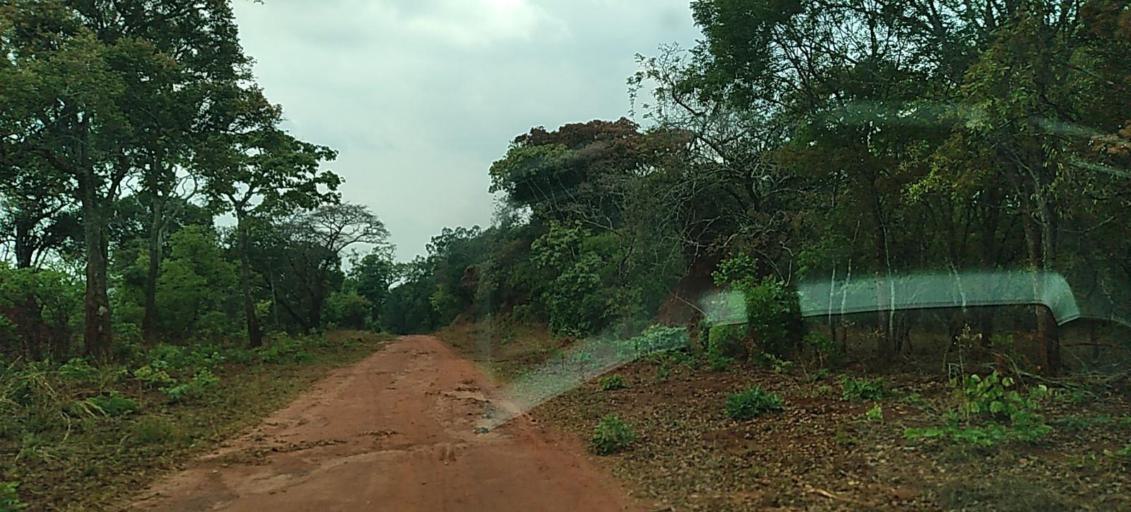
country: ZM
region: North-Western
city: Mwinilunga
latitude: -11.5429
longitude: 24.7797
